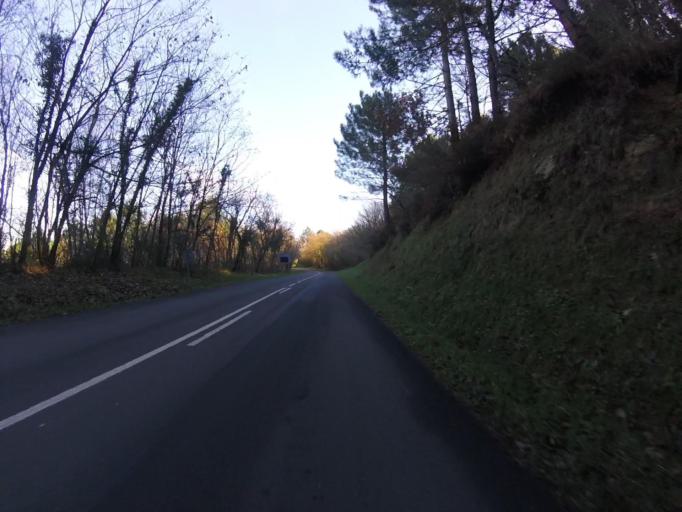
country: ES
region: Basque Country
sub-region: Provincia de Guipuzcoa
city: Fuenterrabia
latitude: 43.3668
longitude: -1.8256
